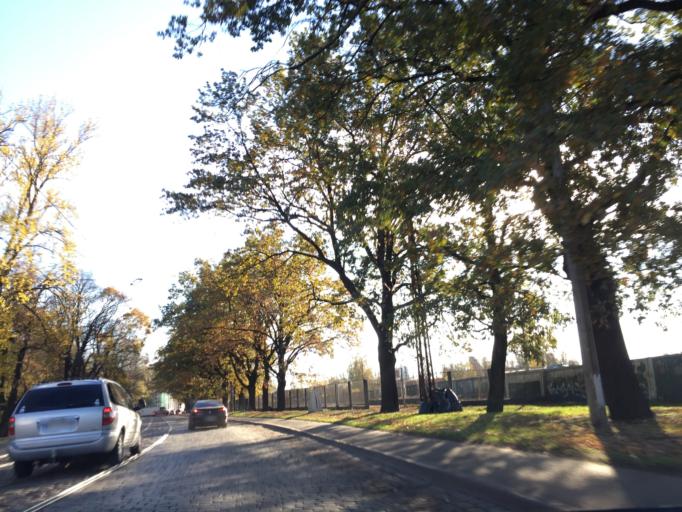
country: LV
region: Riga
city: Riga
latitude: 56.9652
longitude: 24.0978
